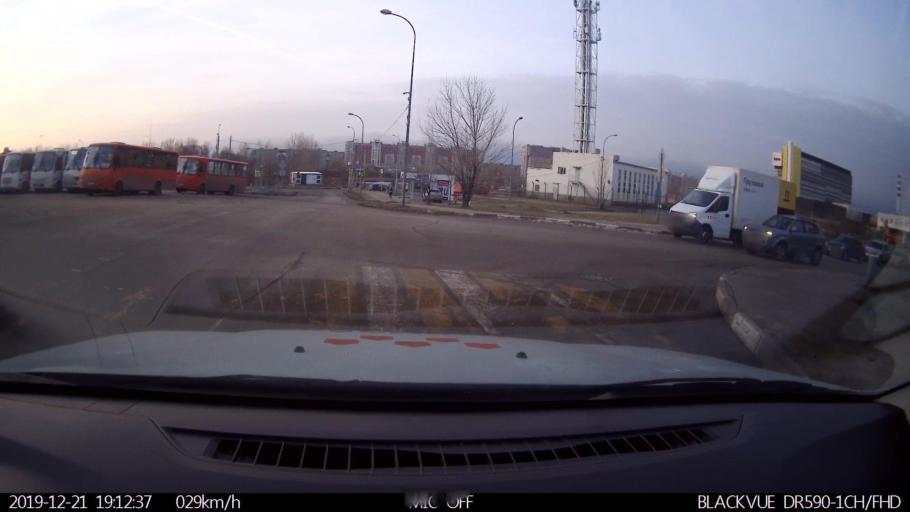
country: RU
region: Nizjnij Novgorod
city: Nizhniy Novgorod
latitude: 56.3384
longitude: 43.9533
